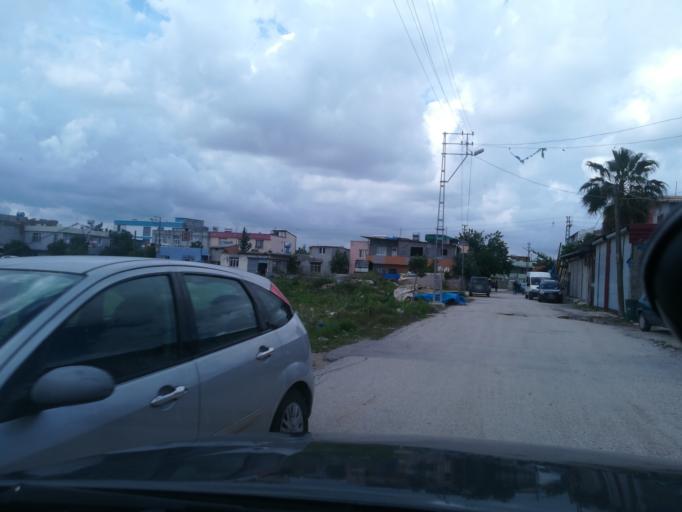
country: TR
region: Adana
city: Yuregir
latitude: 36.9757
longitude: 35.3921
